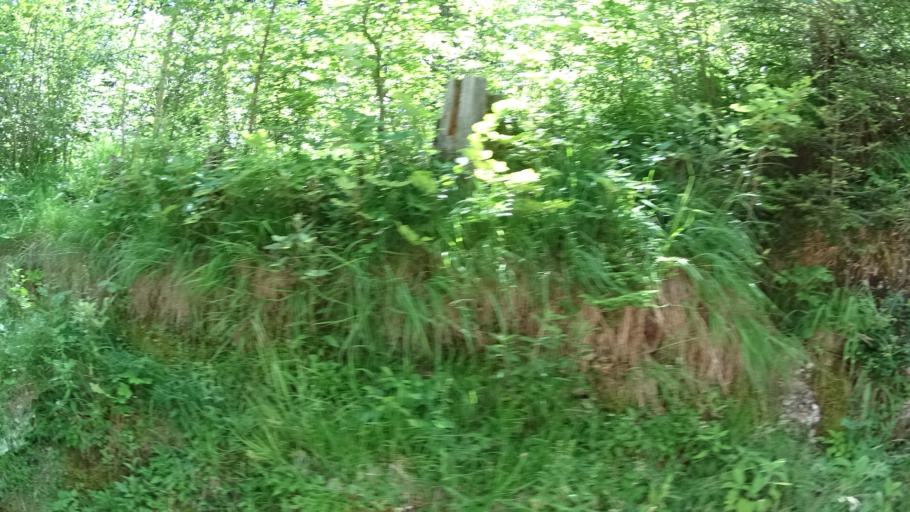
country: CH
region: Lucerne
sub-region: Lucerne-Land District
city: Vitznau
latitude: 47.0277
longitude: 8.4819
